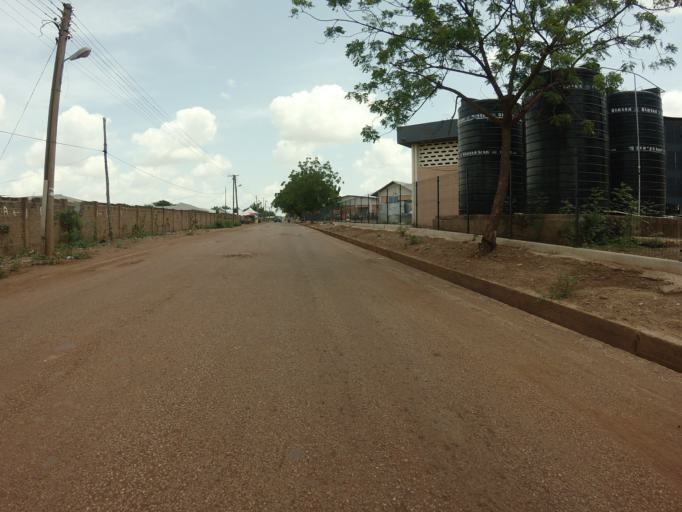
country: GH
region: Northern
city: Tamale
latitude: 9.3925
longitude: -0.8223
